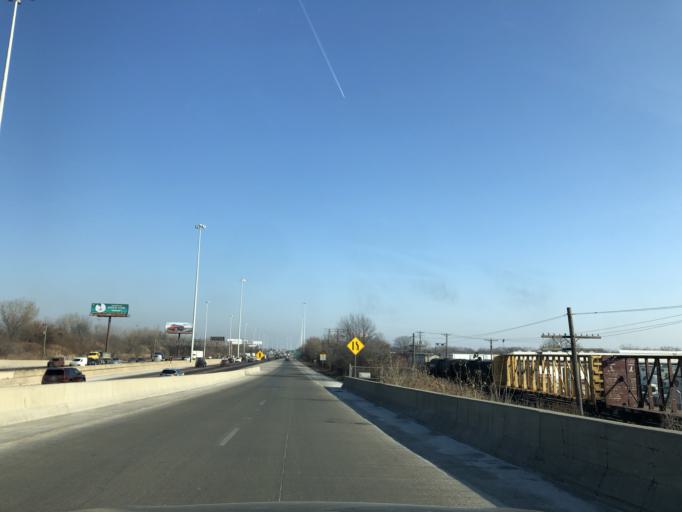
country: US
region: Illinois
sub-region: Cook County
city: Stickney
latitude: 41.8113
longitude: -87.7606
